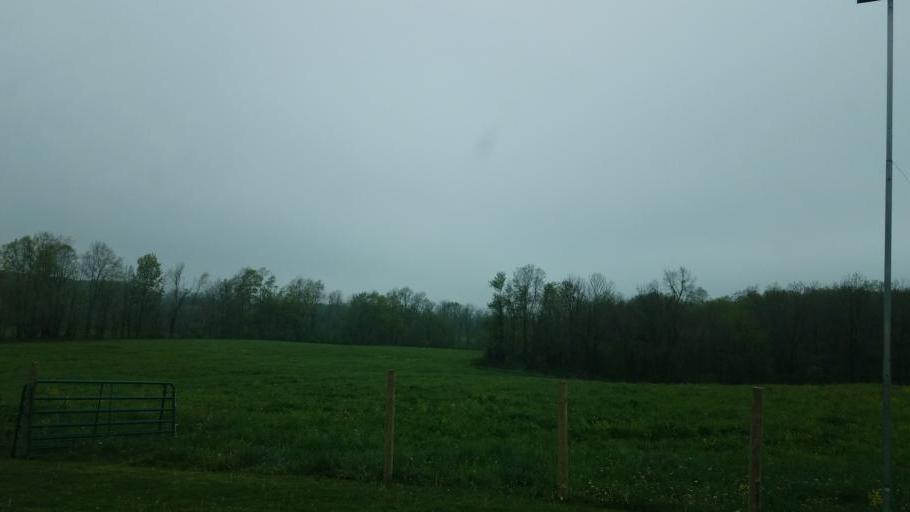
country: US
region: Ohio
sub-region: Knox County
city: Fredericktown
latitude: 40.5264
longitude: -82.6673
